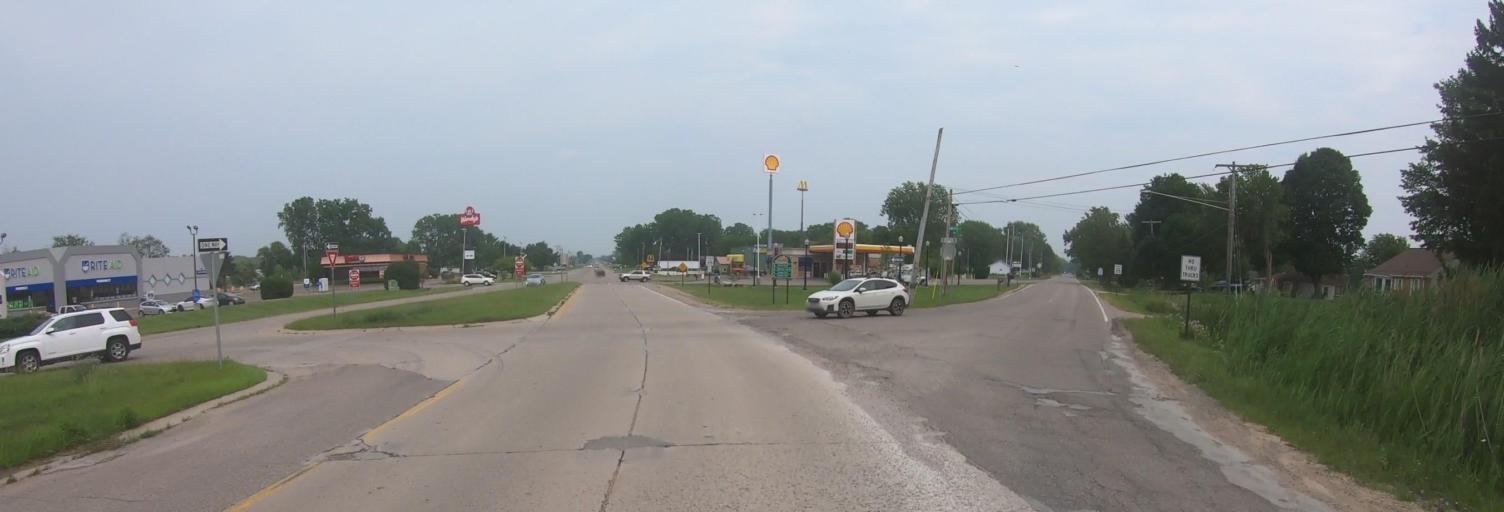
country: US
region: Michigan
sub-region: Shiawassee County
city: Durand
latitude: 42.9251
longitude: -83.9981
